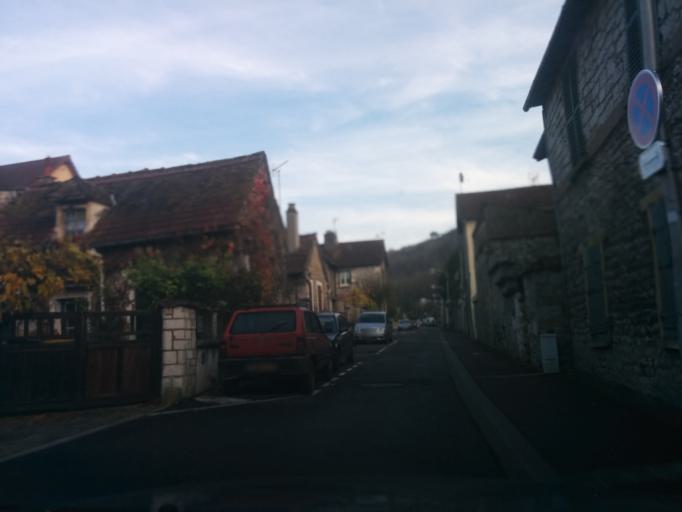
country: FR
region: Haute-Normandie
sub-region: Departement de l'Eure
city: Vernon
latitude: 49.0985
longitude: 1.4944
